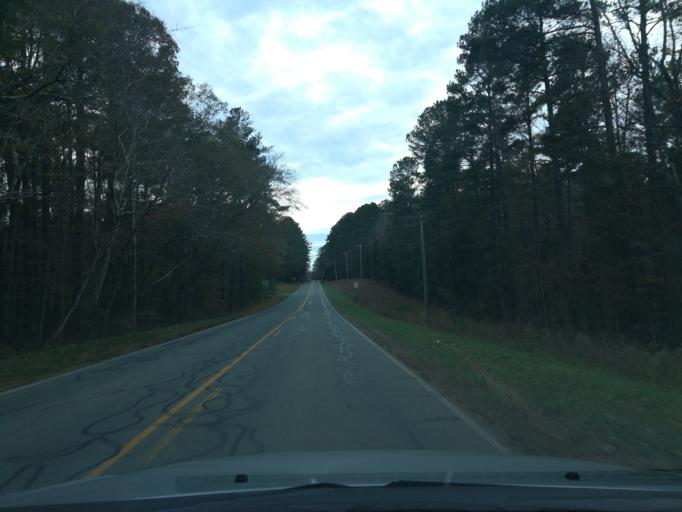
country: US
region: North Carolina
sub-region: Orange County
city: Chapel Hill
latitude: 35.9934
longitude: -79.0629
